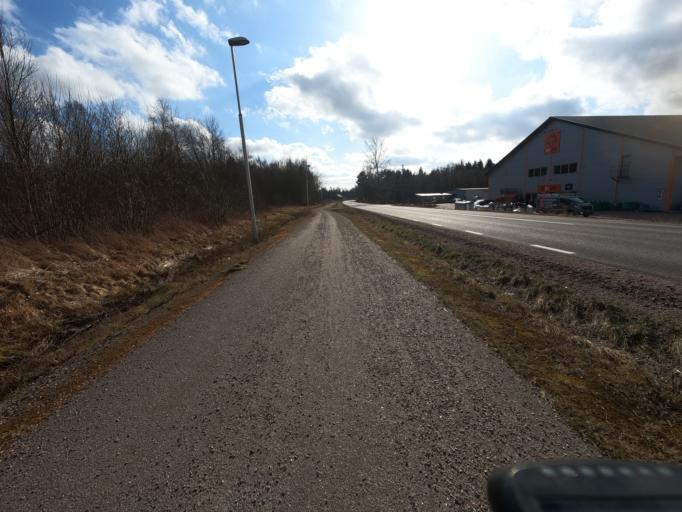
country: SE
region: Kronoberg
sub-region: Alvesta Kommun
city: Vislanda
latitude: 56.7438
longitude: 14.5514
